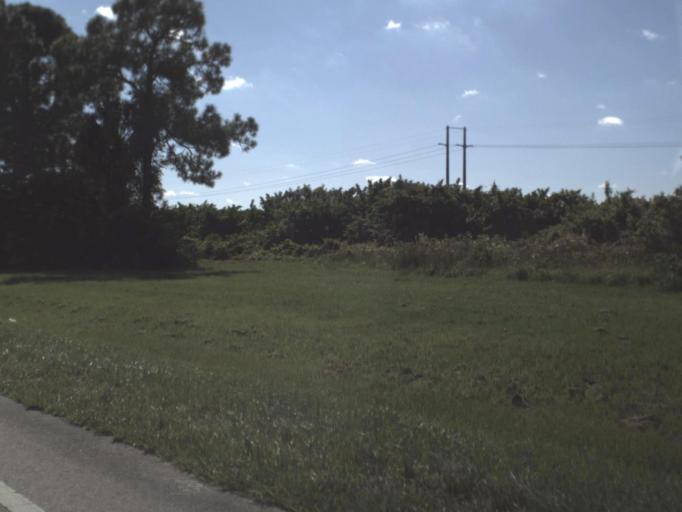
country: US
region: Florida
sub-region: Collier County
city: Immokalee
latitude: 26.4994
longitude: -81.4890
